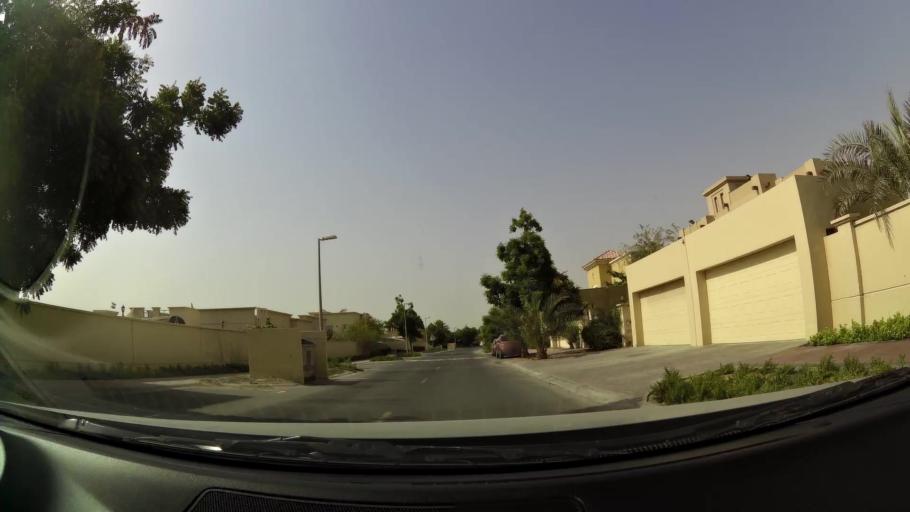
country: AE
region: Ash Shariqah
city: Sharjah
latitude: 25.2660
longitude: 55.4568
